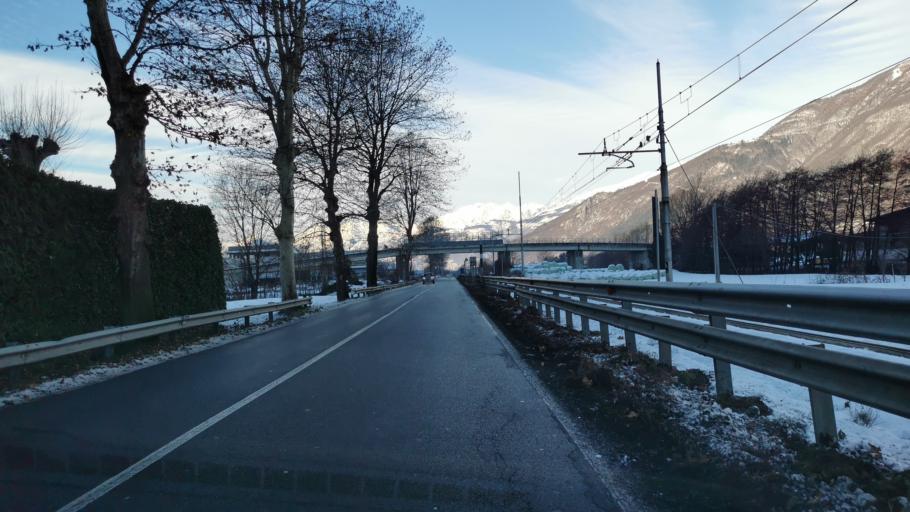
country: IT
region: Lombardy
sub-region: Provincia di Sondrio
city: Rogolo
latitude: 46.1368
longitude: 9.5057
